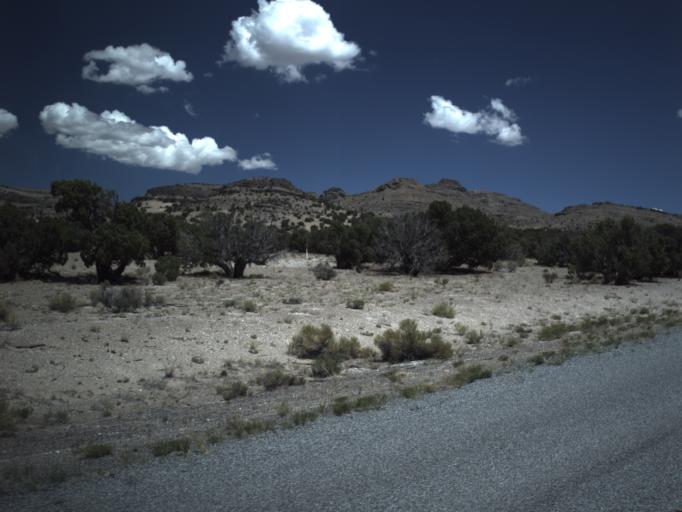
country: US
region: Utah
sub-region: Beaver County
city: Milford
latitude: 39.0743
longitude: -113.7167
